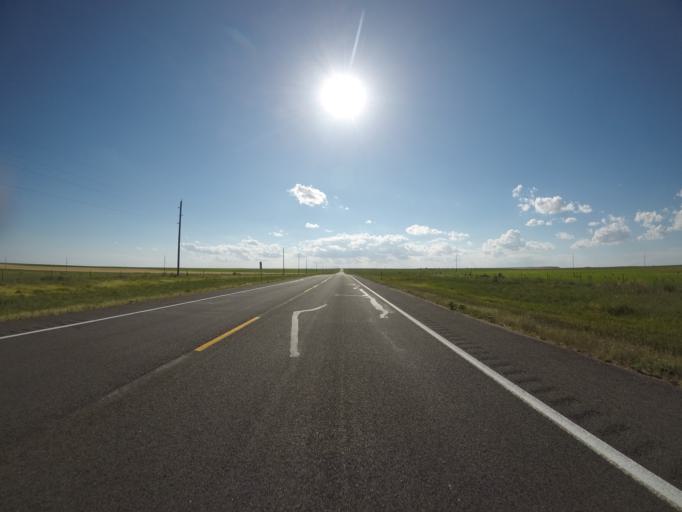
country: US
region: Colorado
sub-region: Morgan County
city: Fort Morgan
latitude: 40.6107
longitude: -103.7503
